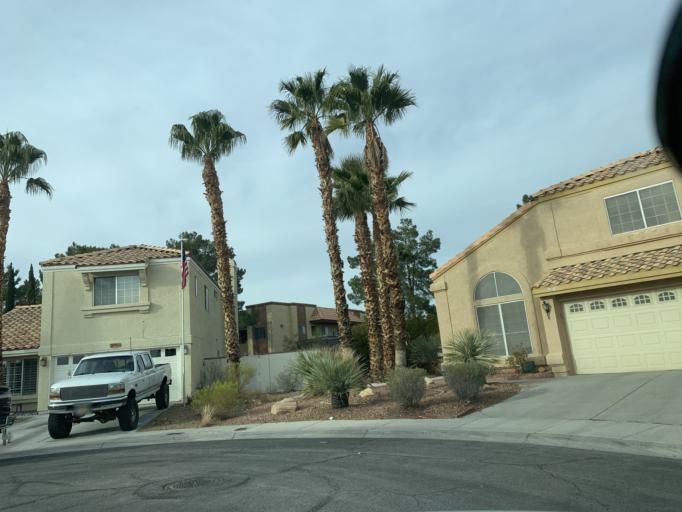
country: US
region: Nevada
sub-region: Clark County
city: Summerlin South
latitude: 36.1424
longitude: -115.3024
